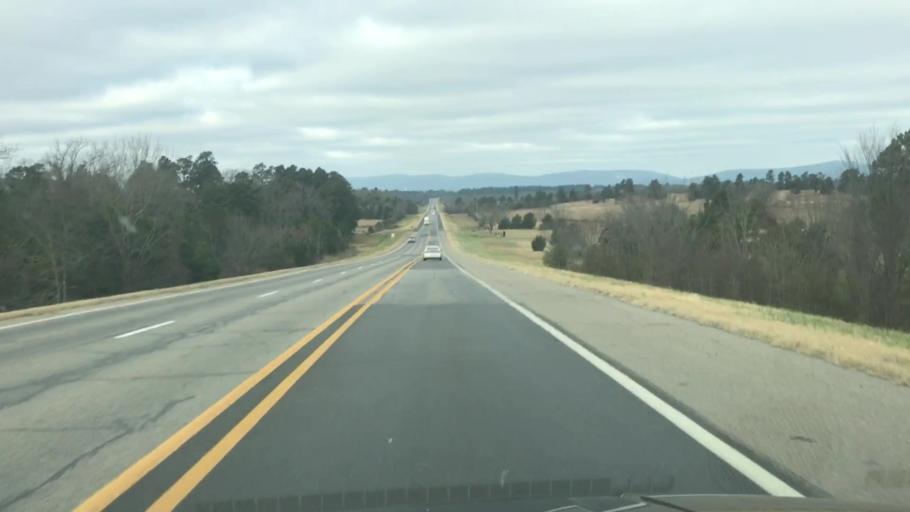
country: US
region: Arkansas
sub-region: Scott County
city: Waldron
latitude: 34.8677
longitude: -94.0781
